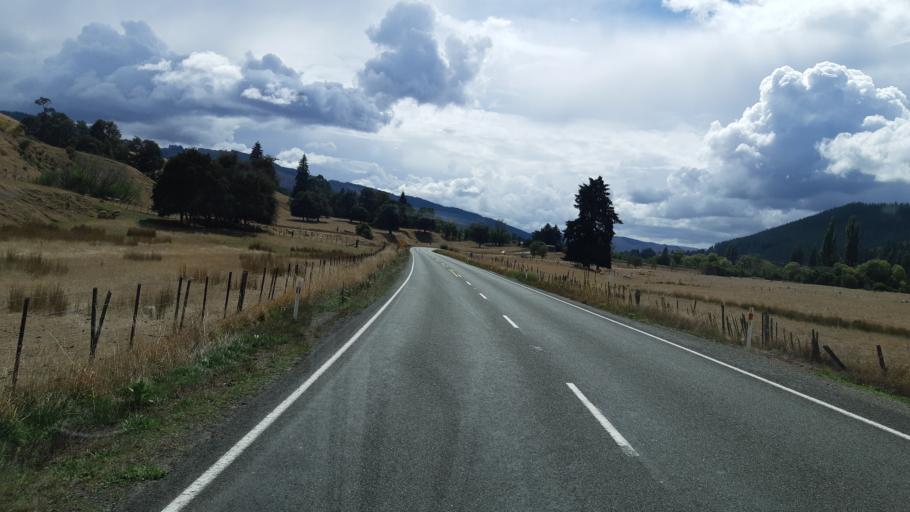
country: NZ
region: Tasman
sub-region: Tasman District
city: Wakefield
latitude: -41.4851
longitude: 172.7993
